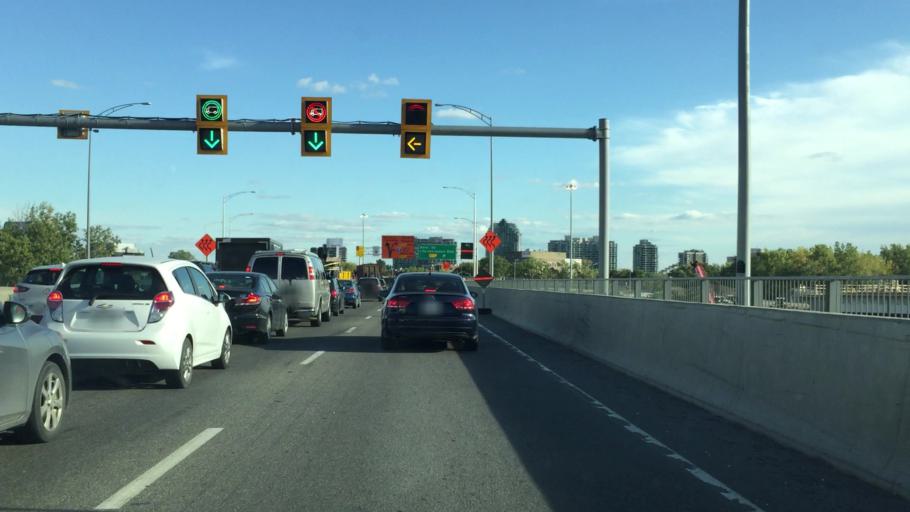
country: CA
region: Quebec
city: Westmount
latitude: 45.4725
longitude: -73.5476
